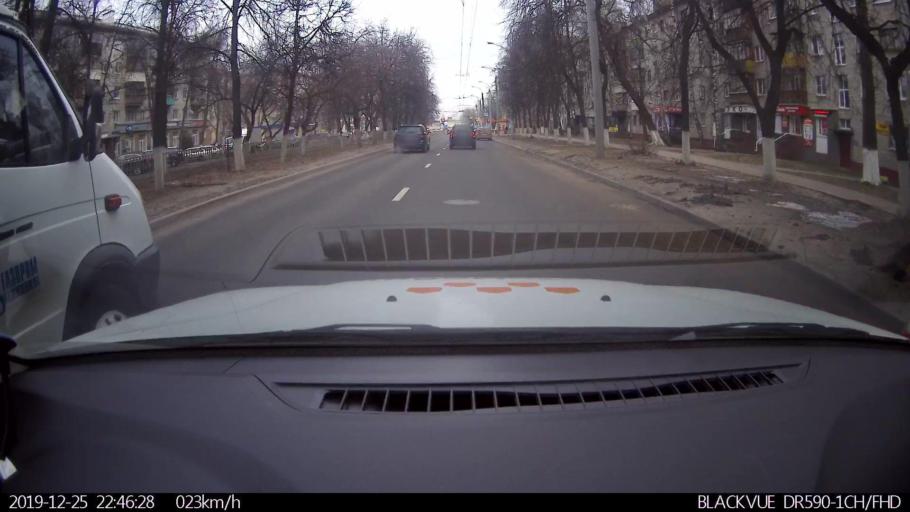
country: RU
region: Nizjnij Novgorod
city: Burevestnik
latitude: 56.2365
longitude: 43.8655
